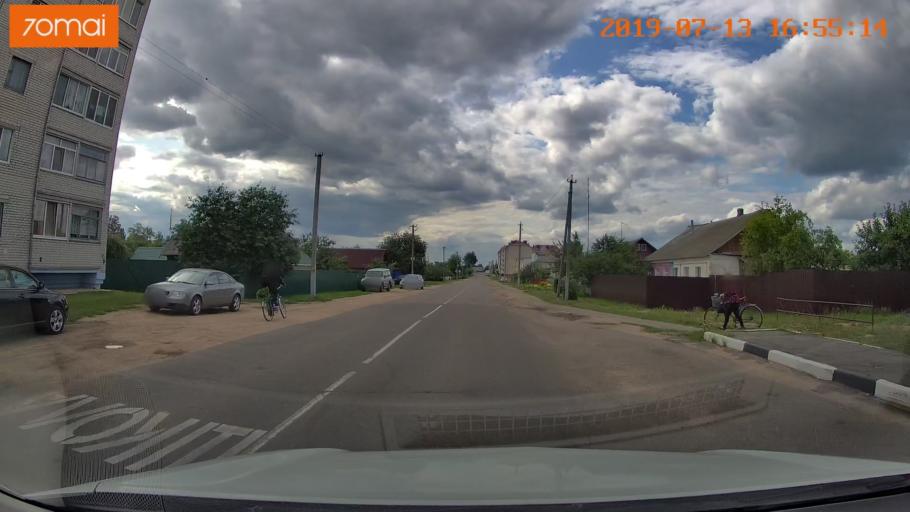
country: BY
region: Mogilev
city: Kirawsk
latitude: 53.2667
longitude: 29.4693
